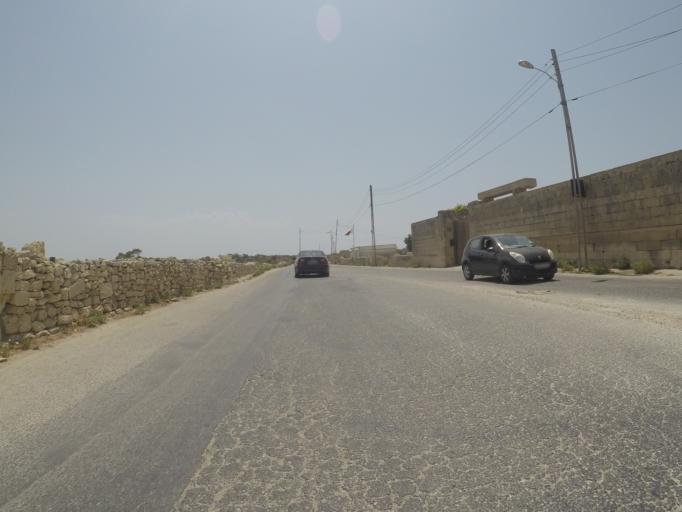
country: MT
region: Is-Siggiewi
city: Siggiewi
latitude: 35.8492
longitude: 14.4335
